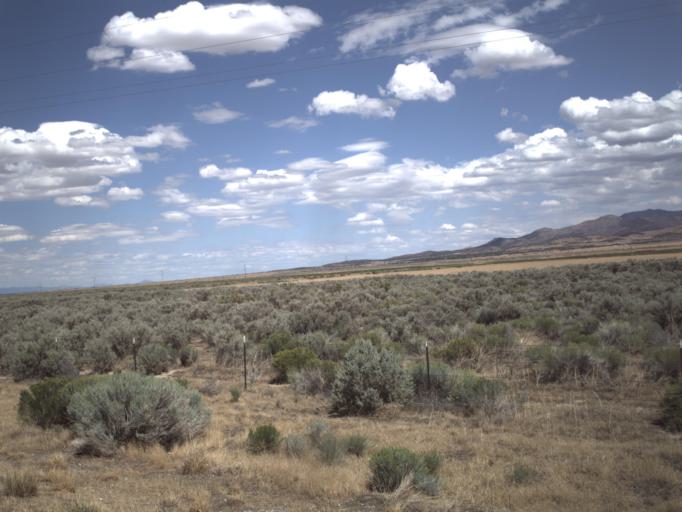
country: US
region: Utah
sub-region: Millard County
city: Delta
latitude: 39.2221
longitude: -112.4215
